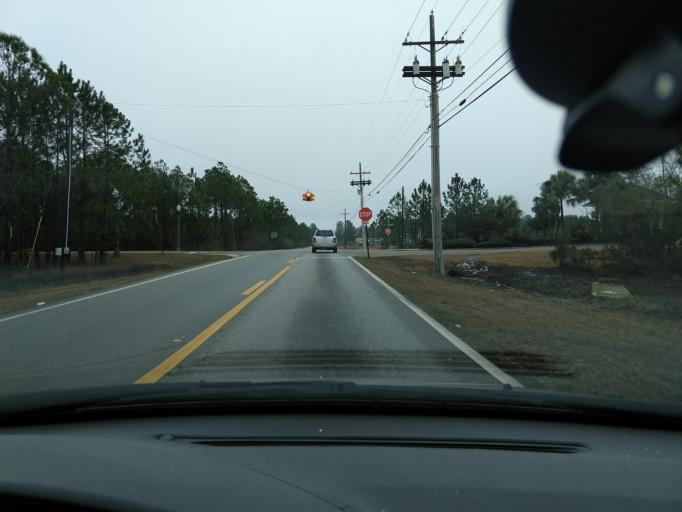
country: US
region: Mississippi
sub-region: Jackson County
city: Gautier
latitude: 30.3928
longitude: -88.6784
